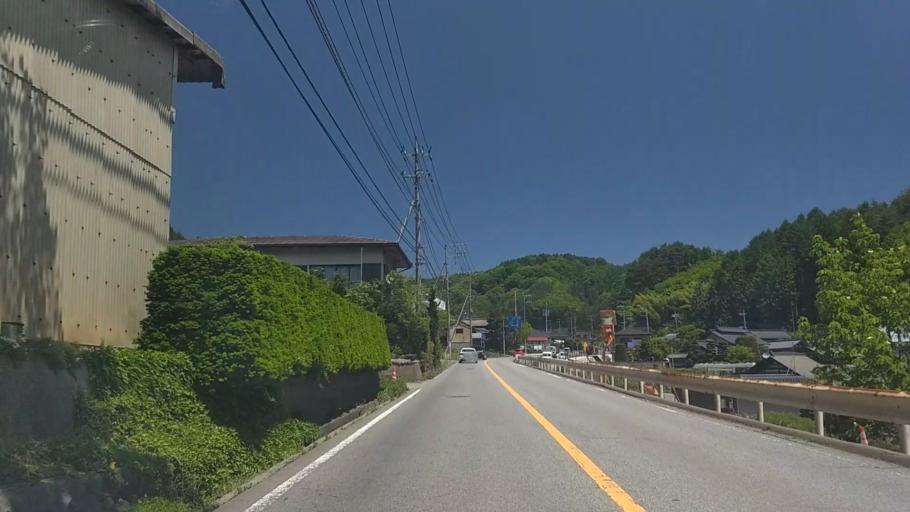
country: JP
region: Yamanashi
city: Nirasaki
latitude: 35.8702
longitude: 138.4275
